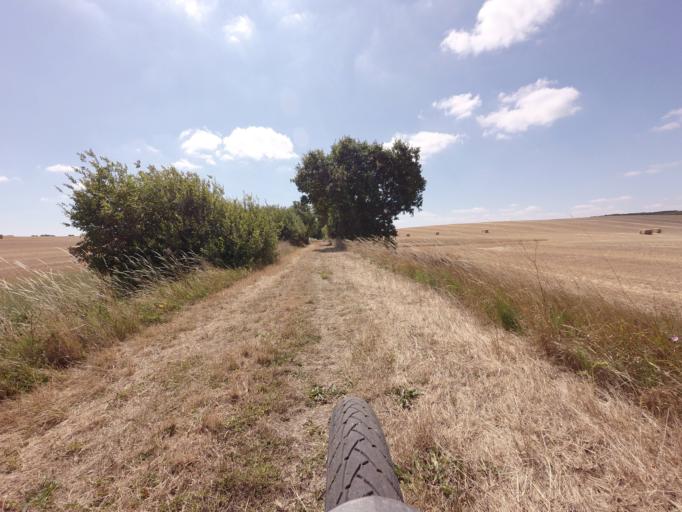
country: DK
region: Central Jutland
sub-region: Odder Kommune
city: Odder
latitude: 55.9197
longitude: 10.1098
